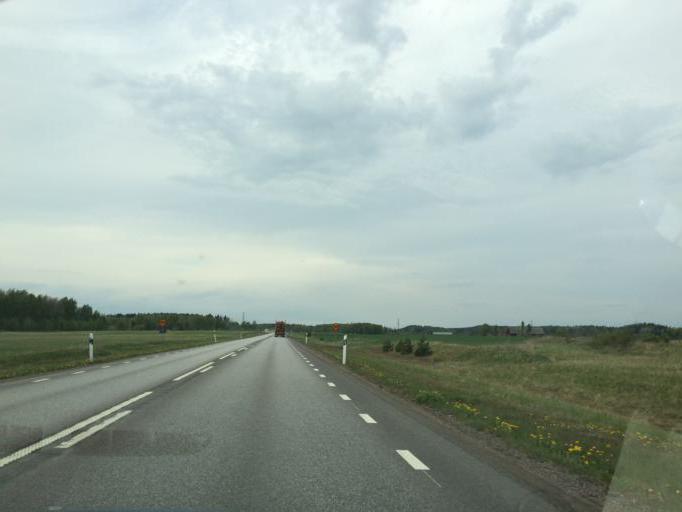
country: SE
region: Vaestmanland
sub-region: Kopings Kommun
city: Koping
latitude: 59.5288
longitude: 15.9595
